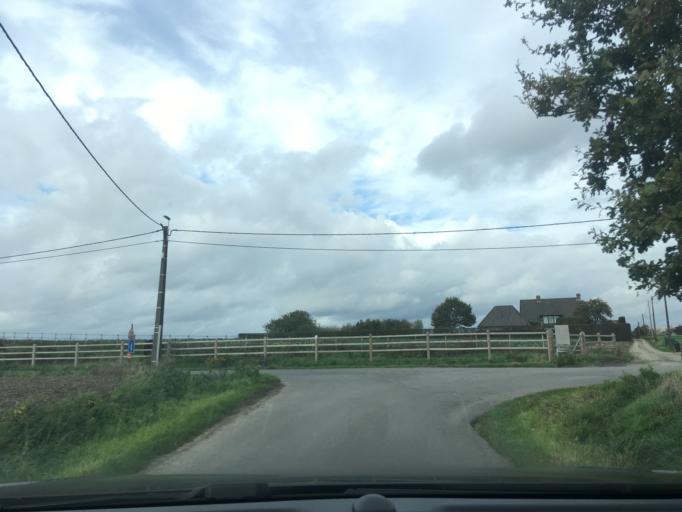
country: BE
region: Flanders
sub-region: Provincie West-Vlaanderen
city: Moorslede
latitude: 50.9110
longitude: 3.0929
